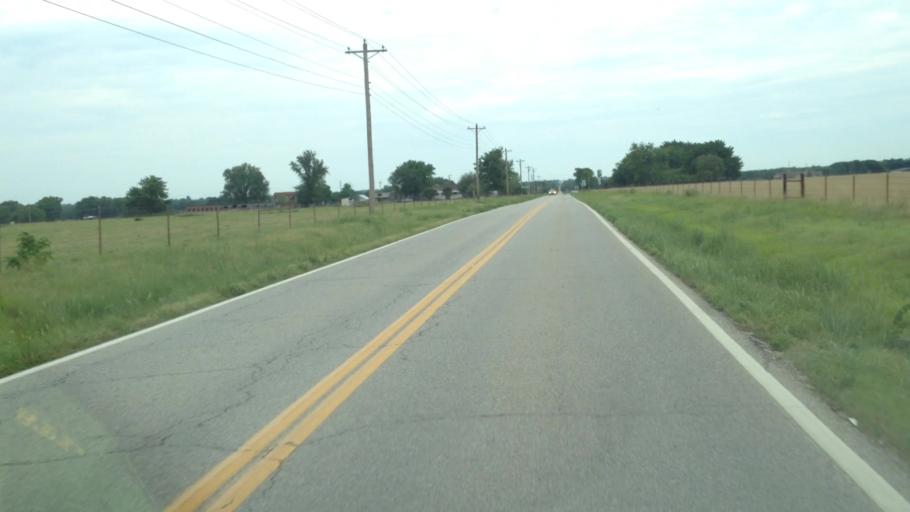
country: US
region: Oklahoma
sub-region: Delaware County
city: Cleora
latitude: 36.6086
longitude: -94.9634
